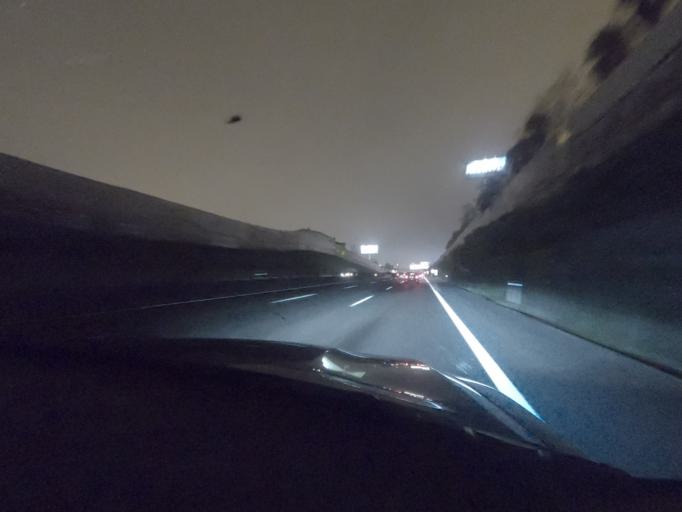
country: PT
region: Lisbon
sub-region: Loures
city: Sacavem
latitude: 38.7973
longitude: -9.1105
